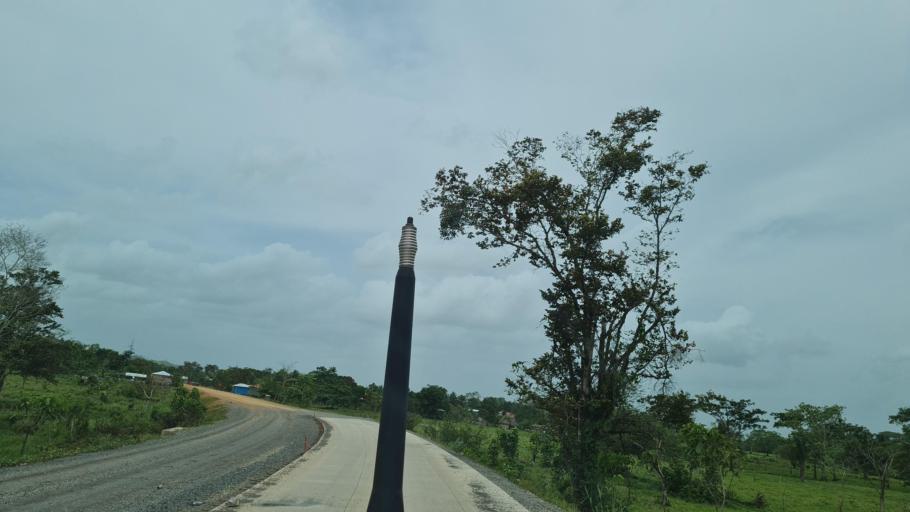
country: NI
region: Atlantico Norte (RAAN)
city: Bonanza
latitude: 14.0409
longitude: -84.0748
